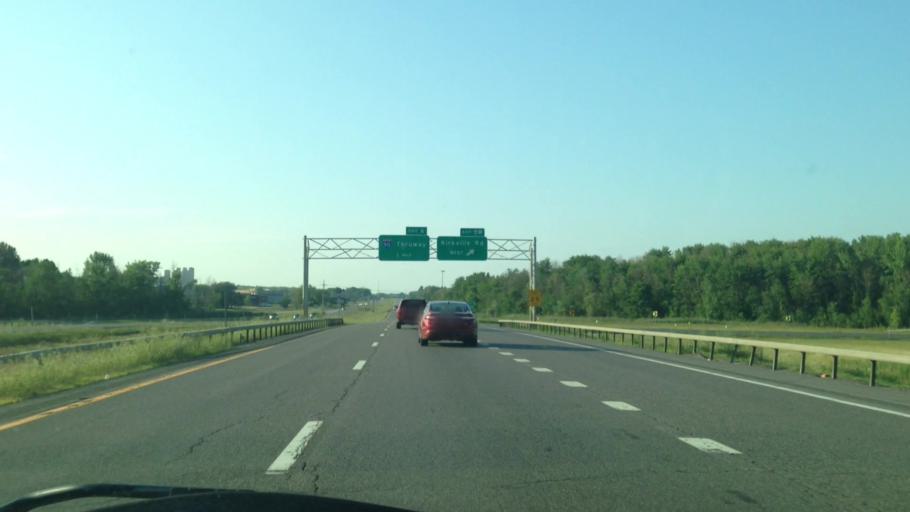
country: US
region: New York
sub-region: Onondaga County
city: East Syracuse
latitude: 43.0783
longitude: -76.0534
